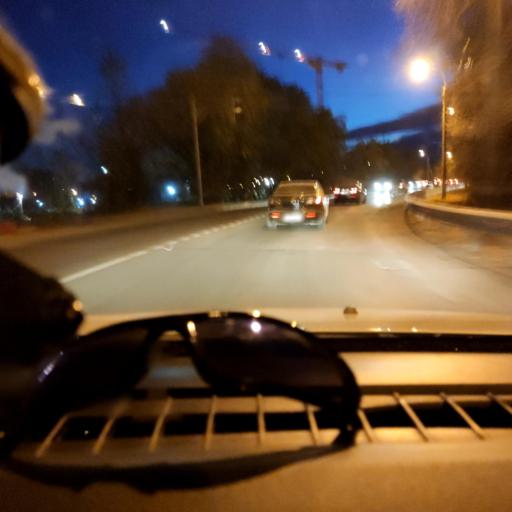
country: RU
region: Samara
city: Rozhdestveno
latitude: 53.1597
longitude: 50.0756
